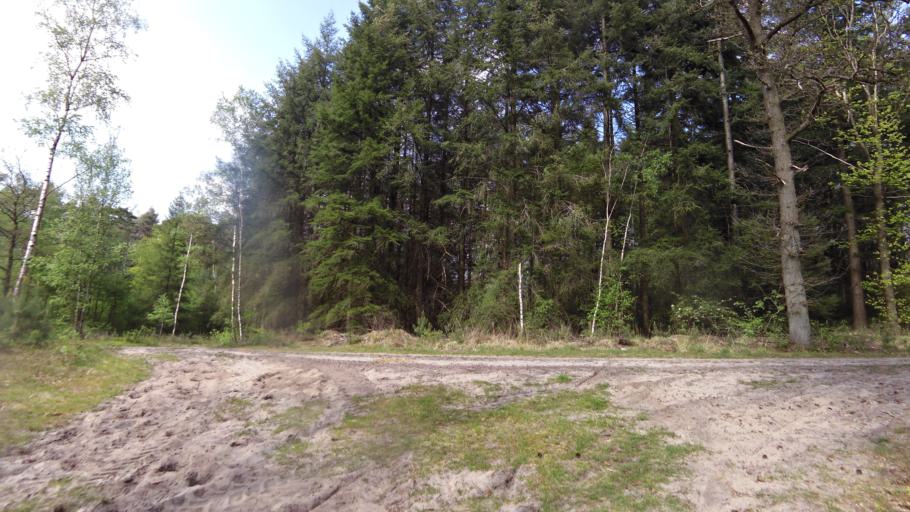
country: NL
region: Gelderland
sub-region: Gemeente Renkum
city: Heelsum
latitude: 52.0159
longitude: 5.7416
